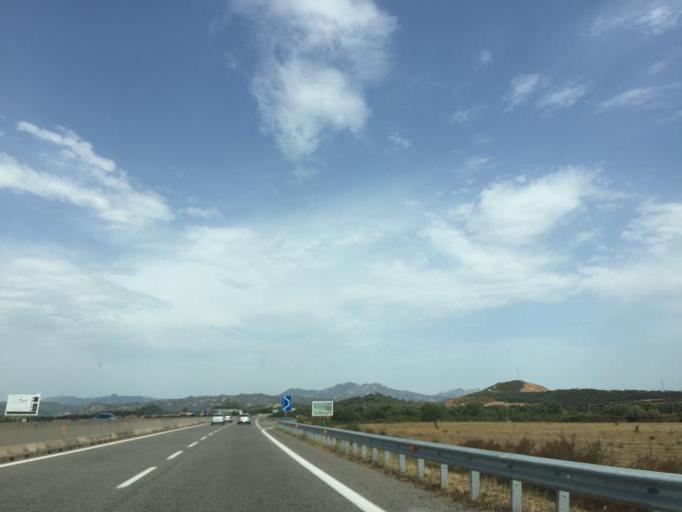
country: IT
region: Sardinia
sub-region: Provincia di Olbia-Tempio
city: Loiri Porto San Paolo
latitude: 40.8654
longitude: 9.5191
